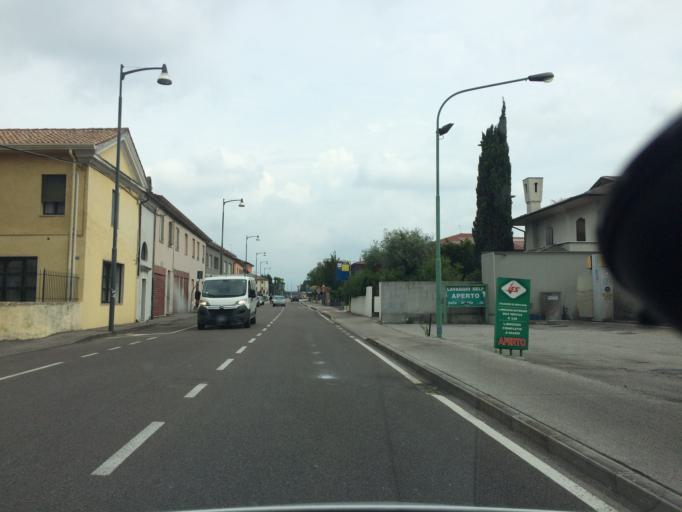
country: IT
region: Veneto
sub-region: Provincia di Padova
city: Cittadella
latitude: 45.6552
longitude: 11.7820
